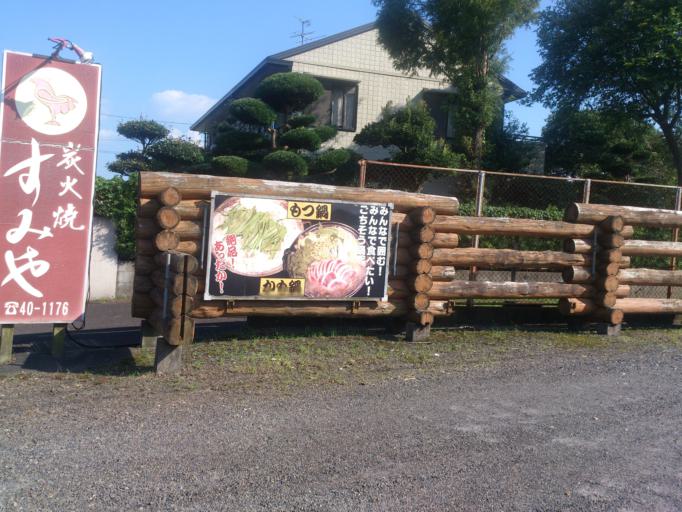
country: JP
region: Kagoshima
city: Kanoya
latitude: 31.3611
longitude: 130.8720
